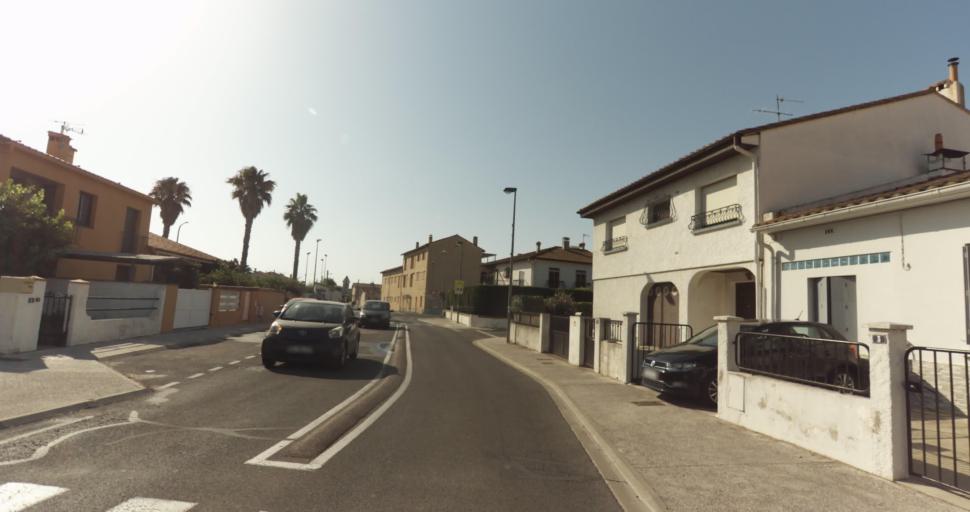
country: FR
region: Languedoc-Roussillon
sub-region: Departement des Pyrenees-Orientales
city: Alenya
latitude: 42.6412
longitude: 2.9812
